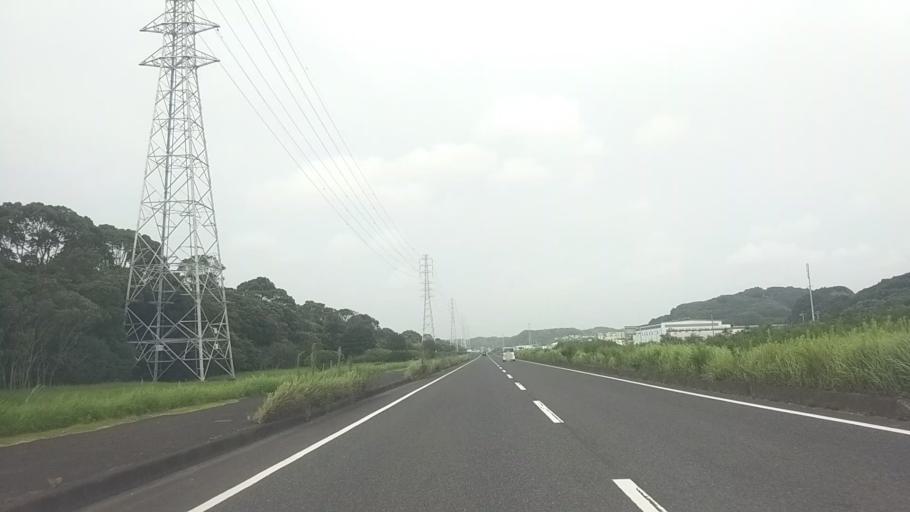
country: JP
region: Chiba
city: Kimitsu
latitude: 35.3483
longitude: 139.8907
